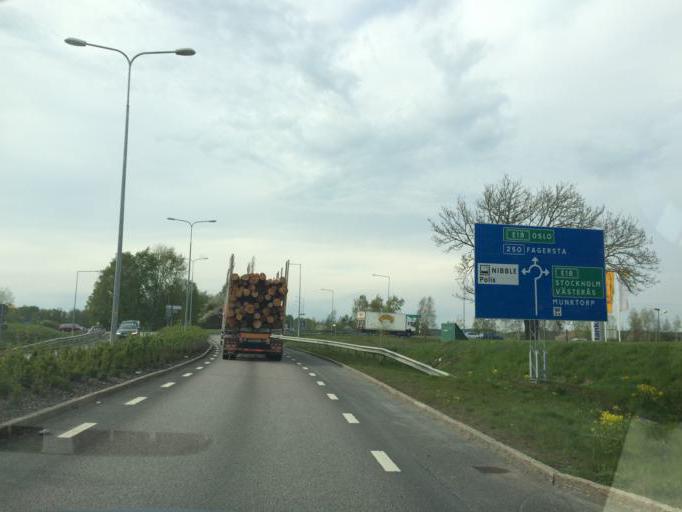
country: SE
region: Vaestmanland
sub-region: Kopings Kommun
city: Koping
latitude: 59.5188
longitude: 15.9721
